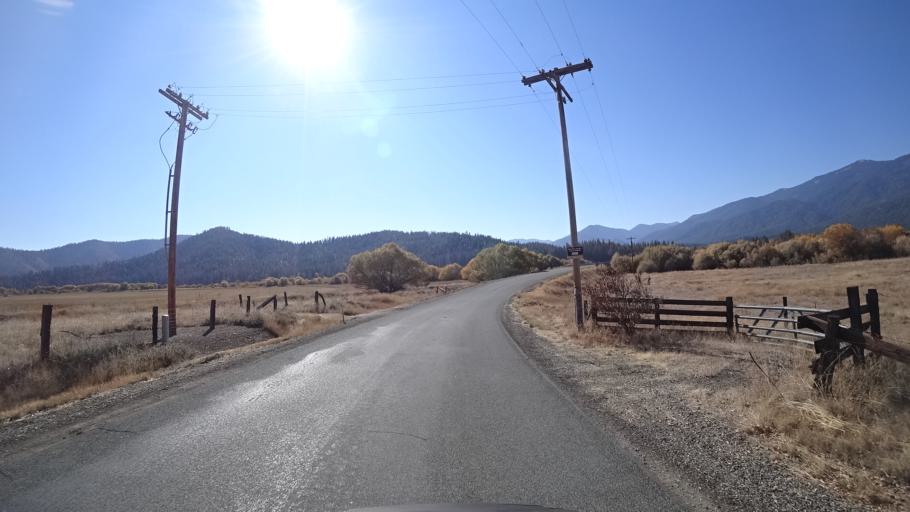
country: US
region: California
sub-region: Siskiyou County
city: Yreka
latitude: 41.6305
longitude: -122.9554
